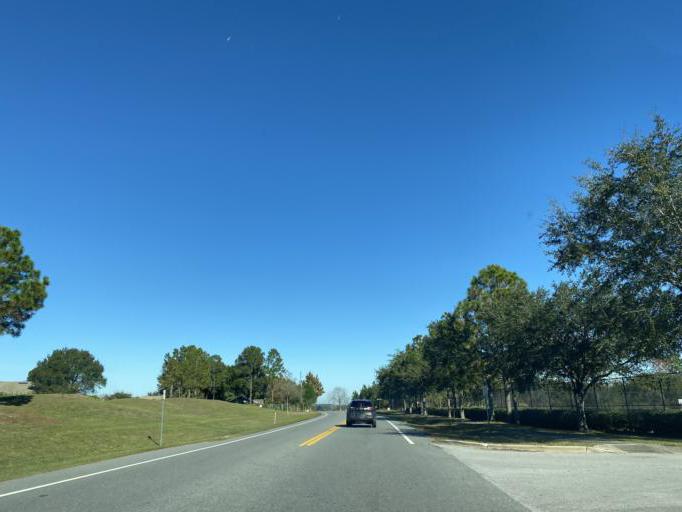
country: US
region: Florida
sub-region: Lake County
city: Minneola
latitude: 28.5203
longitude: -81.7070
